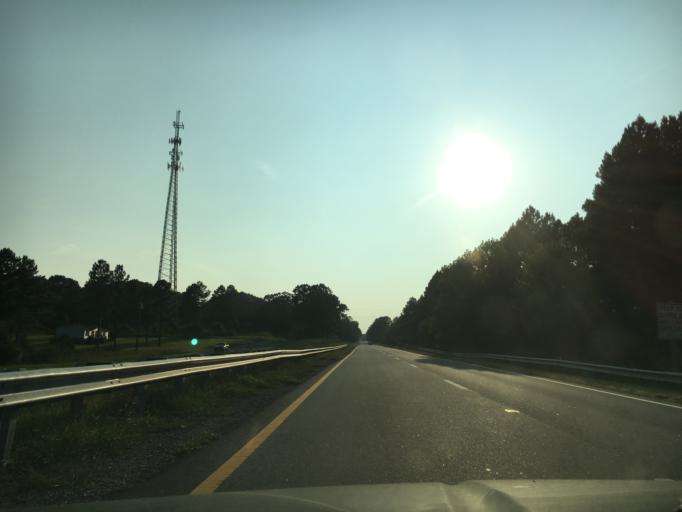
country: US
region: Virginia
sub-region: Prince Edward County
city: Hampden Sydney
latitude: 37.2963
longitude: -78.5852
